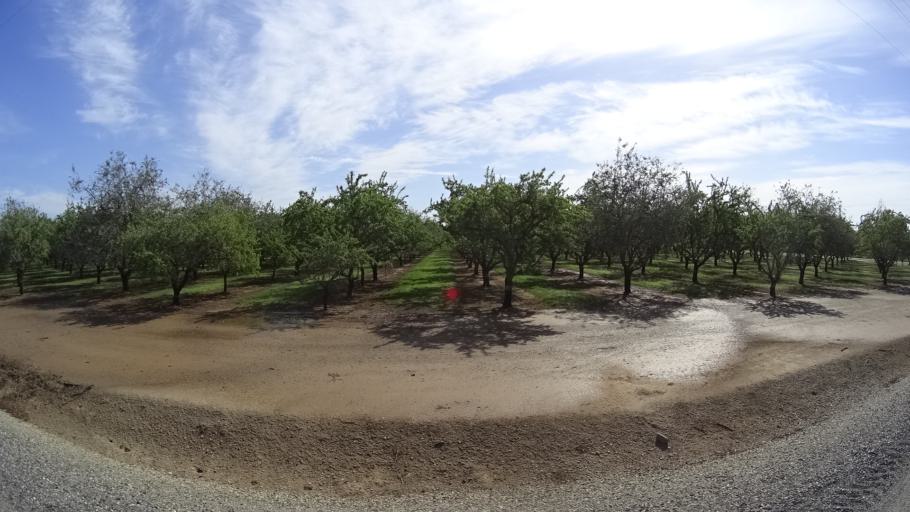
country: US
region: California
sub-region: Glenn County
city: Hamilton City
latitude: 39.6560
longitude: -122.0080
